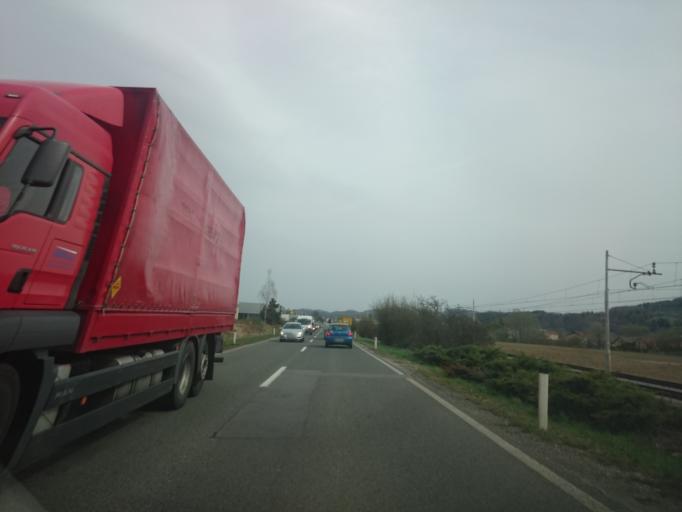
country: SI
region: Sentjur pri Celju
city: Sentjur
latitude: 46.2141
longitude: 15.3854
